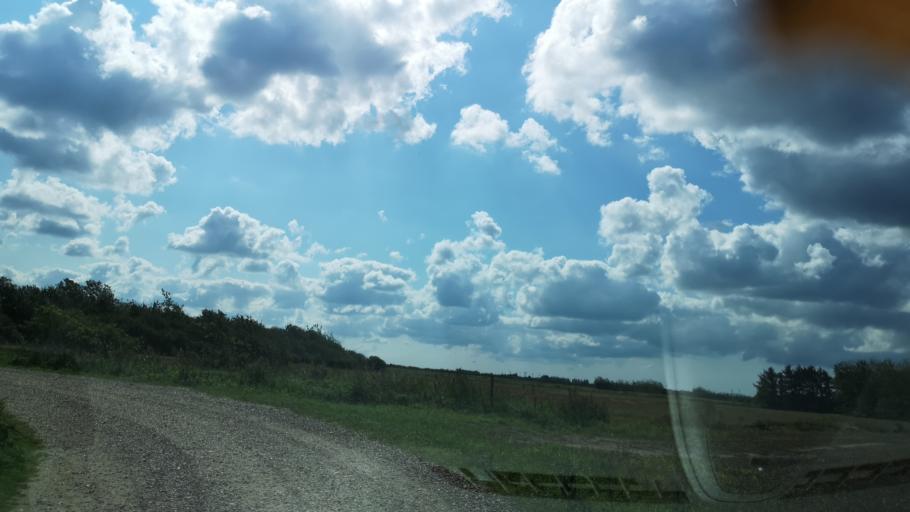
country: DK
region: Central Jutland
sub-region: Ringkobing-Skjern Kommune
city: Skjern
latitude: 55.9045
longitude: 8.3962
